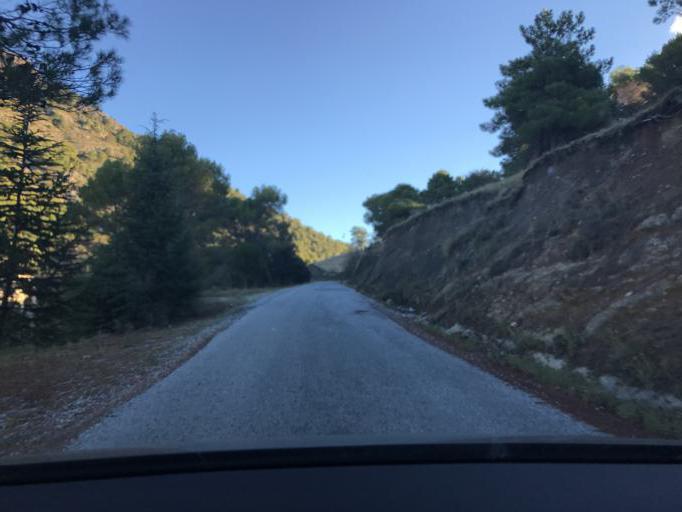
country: ES
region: Andalusia
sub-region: Provincia de Granada
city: Viznar
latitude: 37.2374
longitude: -3.5347
